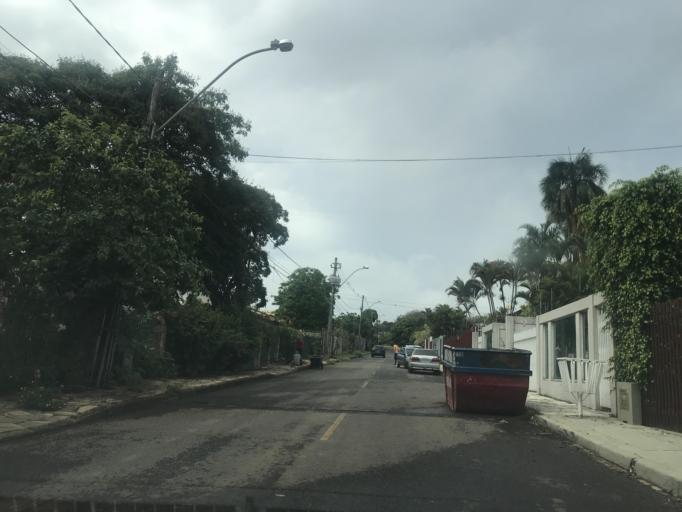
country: BR
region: Federal District
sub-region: Brasilia
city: Brasilia
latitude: -15.8325
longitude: -47.8307
